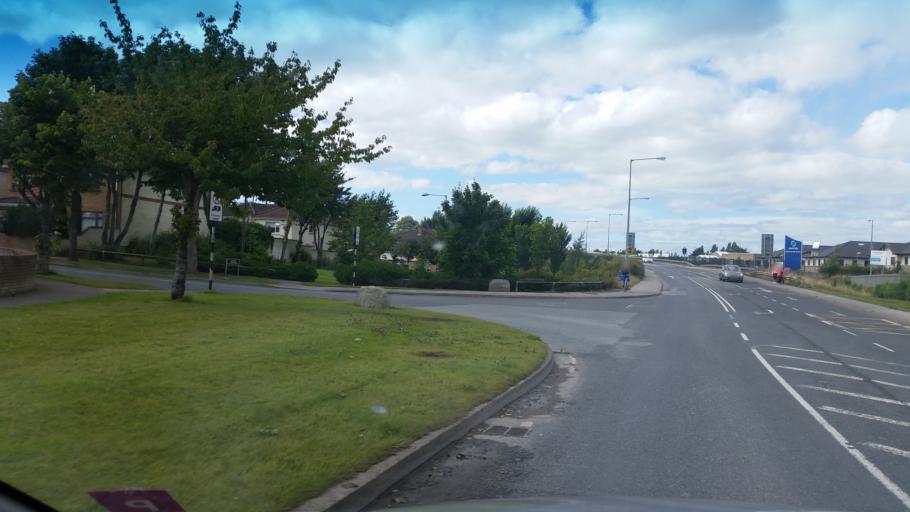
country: IE
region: Leinster
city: Kinsealy-Drinan
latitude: 53.4463
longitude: -6.2006
